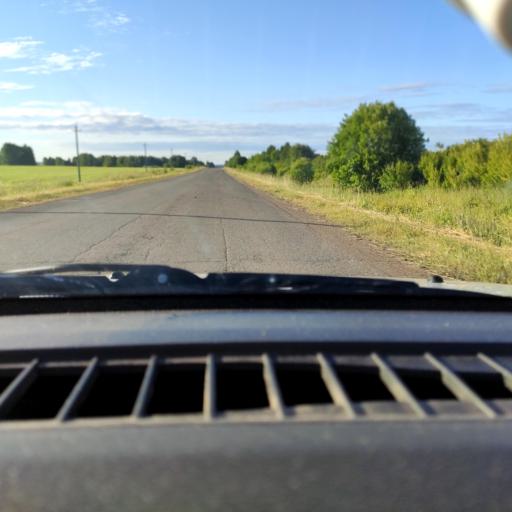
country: RU
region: Perm
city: Uinskoye
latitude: 57.1024
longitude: 56.5385
